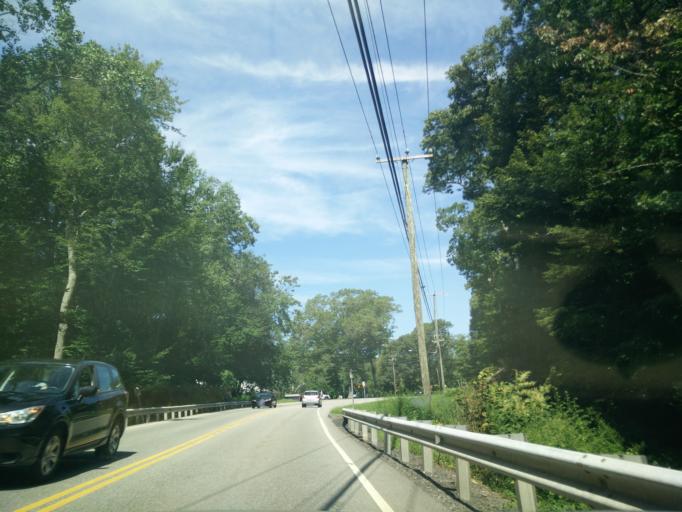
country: US
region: Connecticut
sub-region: Middlesex County
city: Clinton
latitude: 41.3087
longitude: -72.5379
